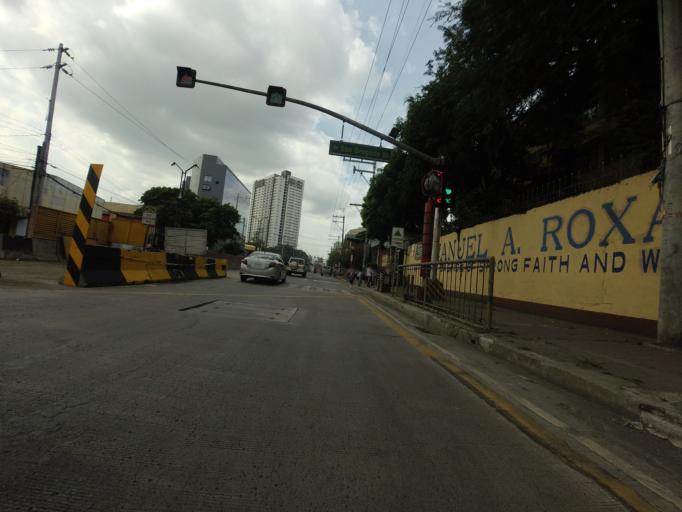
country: PH
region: Metro Manila
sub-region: City of Manila
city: Quiapo
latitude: 14.5819
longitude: 120.9983
